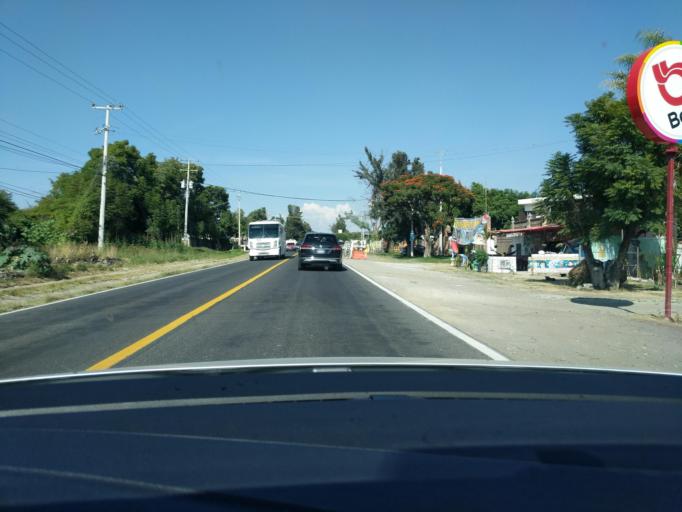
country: MX
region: Puebla
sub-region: Atlixco
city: San Agustin Huixaxtla
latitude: 18.9399
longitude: -98.3991
